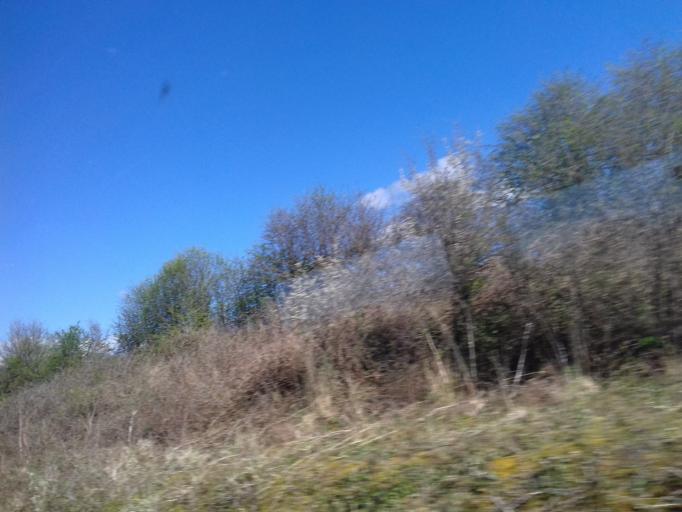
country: IE
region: Munster
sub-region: Ciarrai
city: Cill Airne
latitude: 52.1527
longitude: -9.5863
